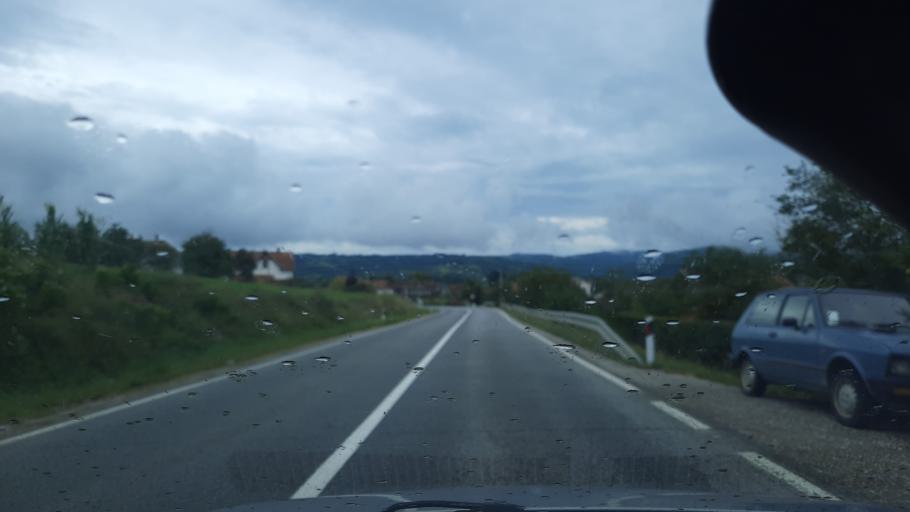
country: RS
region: Central Serbia
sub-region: Sumadijski Okrug
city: Knic
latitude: 43.8989
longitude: 20.7653
